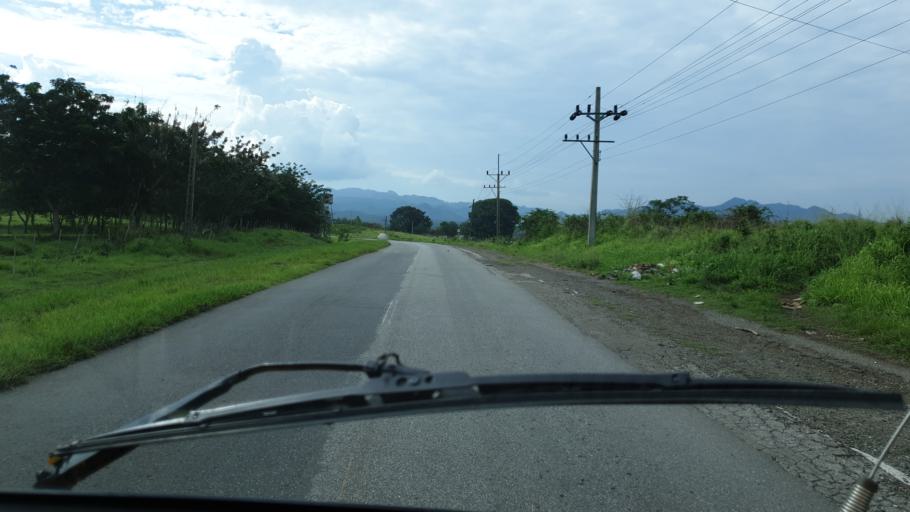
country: CU
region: Cienfuegos
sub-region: Municipio de Cienfuegos
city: Cumanayagua
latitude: 22.0720
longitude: -80.3068
